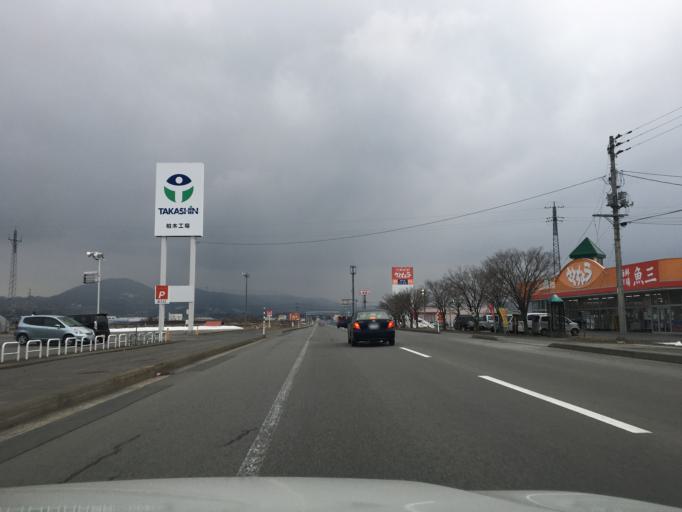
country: JP
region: Aomori
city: Kuroishi
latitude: 40.5825
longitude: 140.5687
